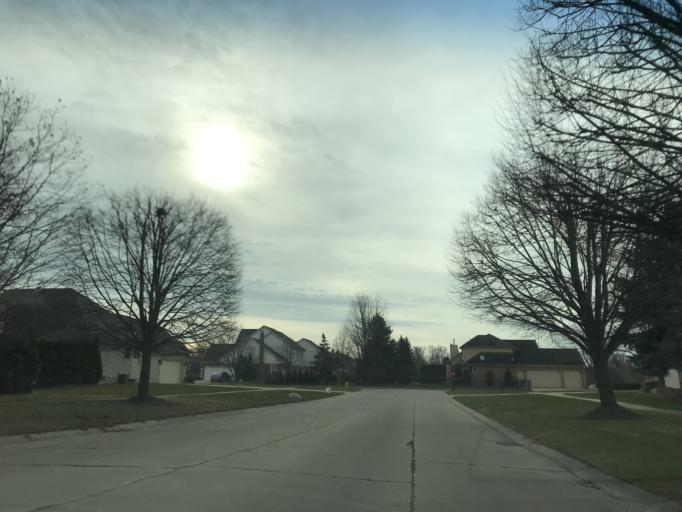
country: US
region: Michigan
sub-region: Macomb County
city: Clinton
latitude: 42.6425
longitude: -82.9203
